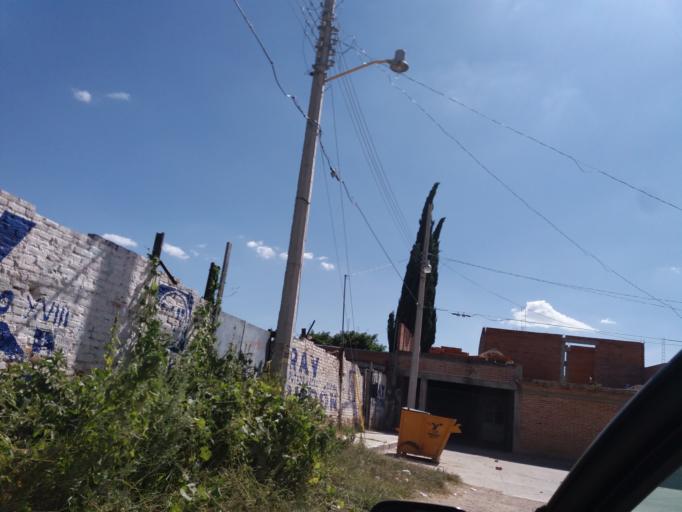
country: MX
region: Aguascalientes
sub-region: Aguascalientes
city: San Sebastian [Fraccionamiento]
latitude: 21.7987
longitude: -102.2734
